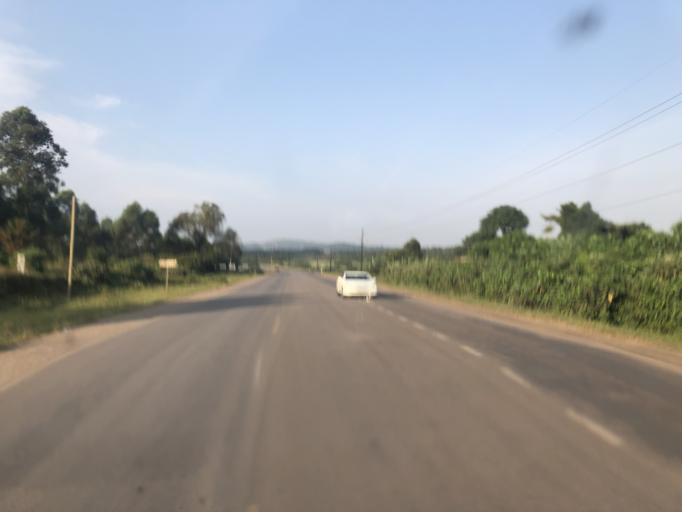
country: UG
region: Central Region
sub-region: Butambala District
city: Gombe
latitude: 0.0872
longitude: 32.1412
